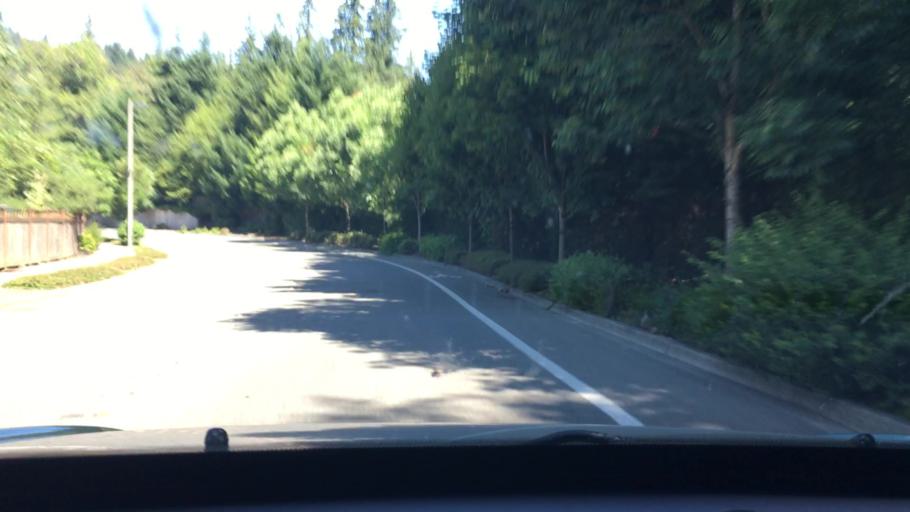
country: US
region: Washington
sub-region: King County
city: Newcastle
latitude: 47.5452
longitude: -122.1276
